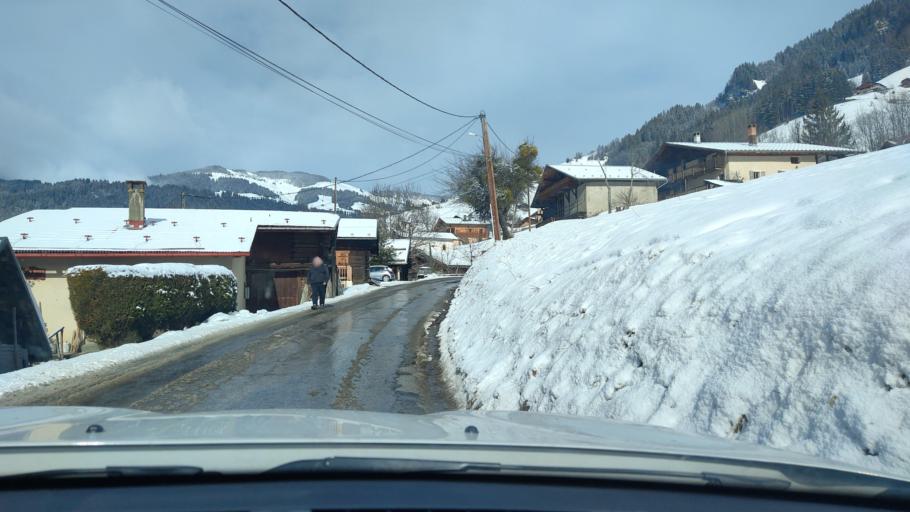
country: FR
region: Rhone-Alpes
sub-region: Departement de la Savoie
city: Beaufort
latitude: 45.7204
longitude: 6.5800
